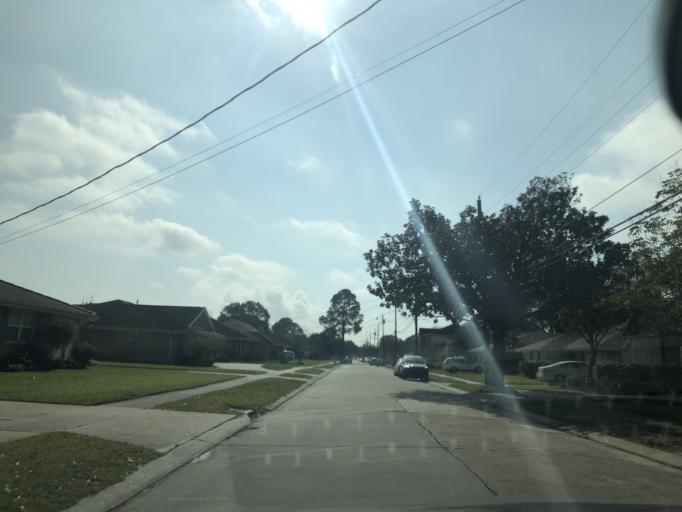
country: US
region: Louisiana
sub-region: Jefferson Parish
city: Metairie
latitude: 29.9959
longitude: -90.1483
